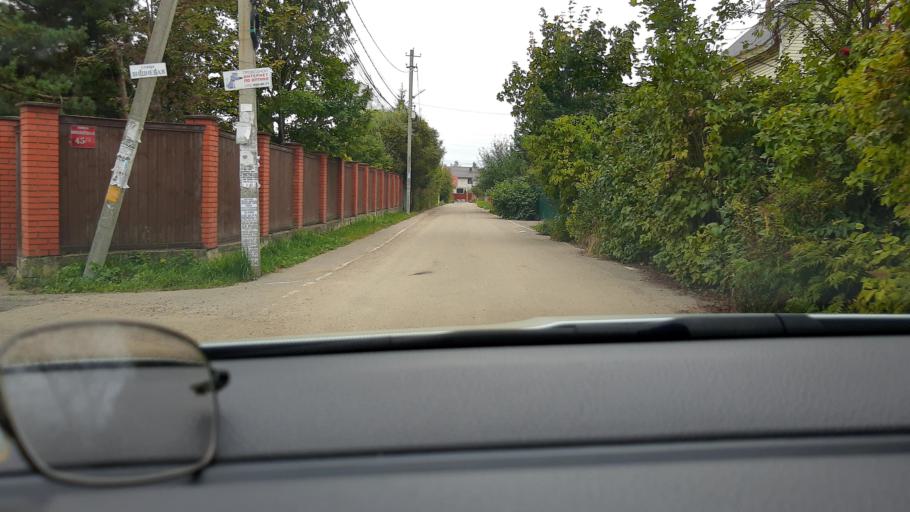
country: RU
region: Moskovskaya
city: Kokoshkino
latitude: 55.5935
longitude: 37.1926
